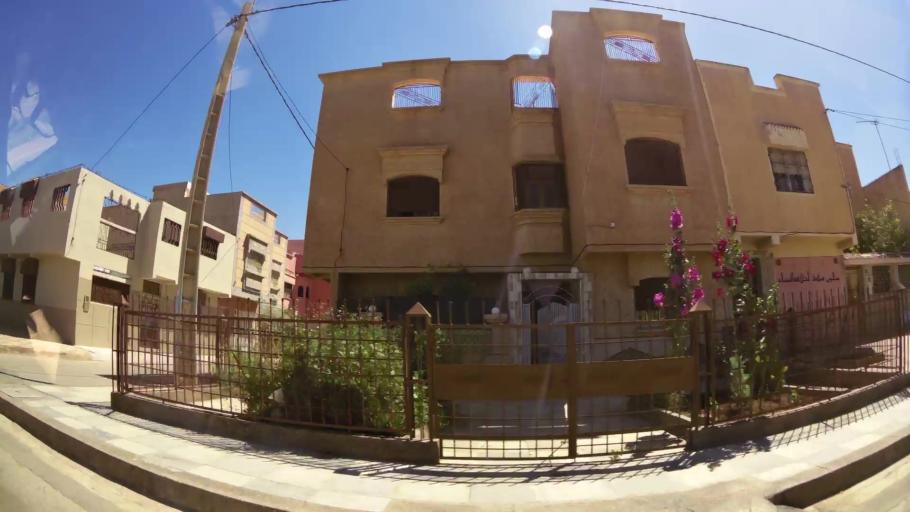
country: MA
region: Oriental
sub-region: Oujda-Angad
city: Oujda
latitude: 34.6624
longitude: -1.9343
